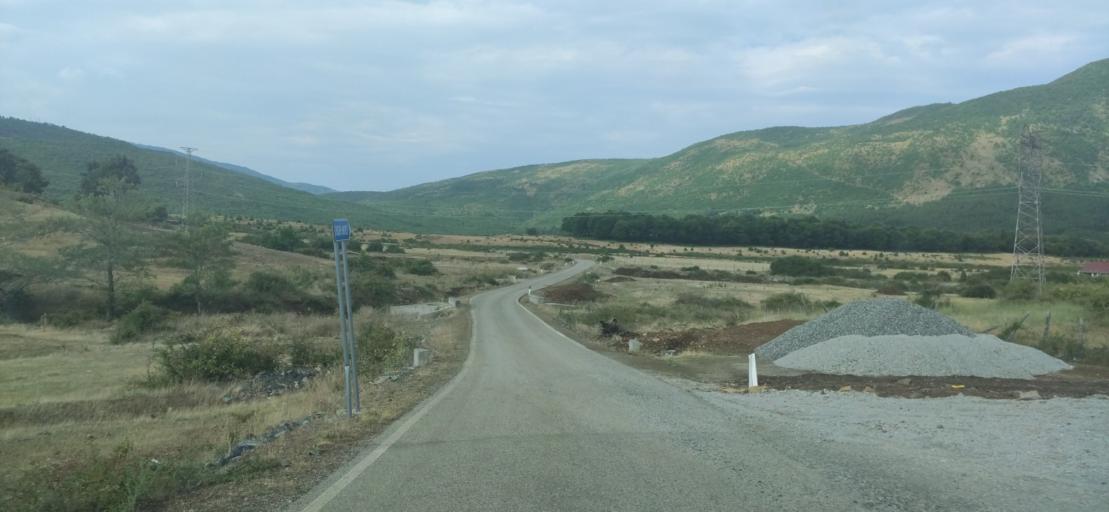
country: AL
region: Shkoder
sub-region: Rrethi i Pukes
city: Iballe
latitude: 42.1865
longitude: 19.9964
